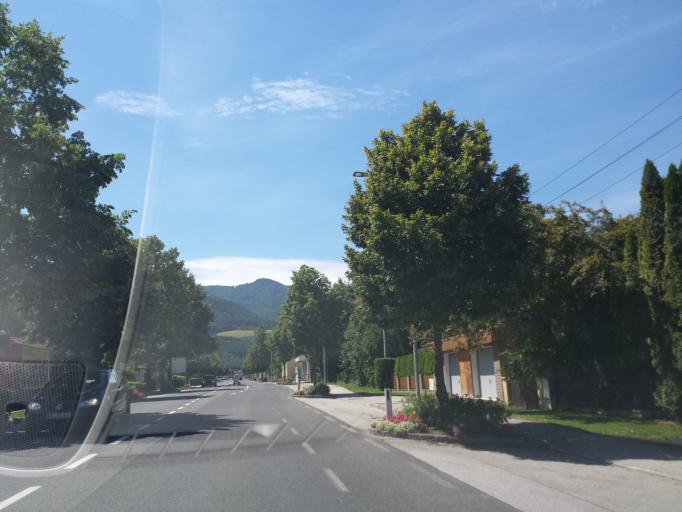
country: AT
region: Lower Austria
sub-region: Politischer Bezirk Neunkirchen
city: Gloggnitz
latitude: 47.6703
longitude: 15.9308
